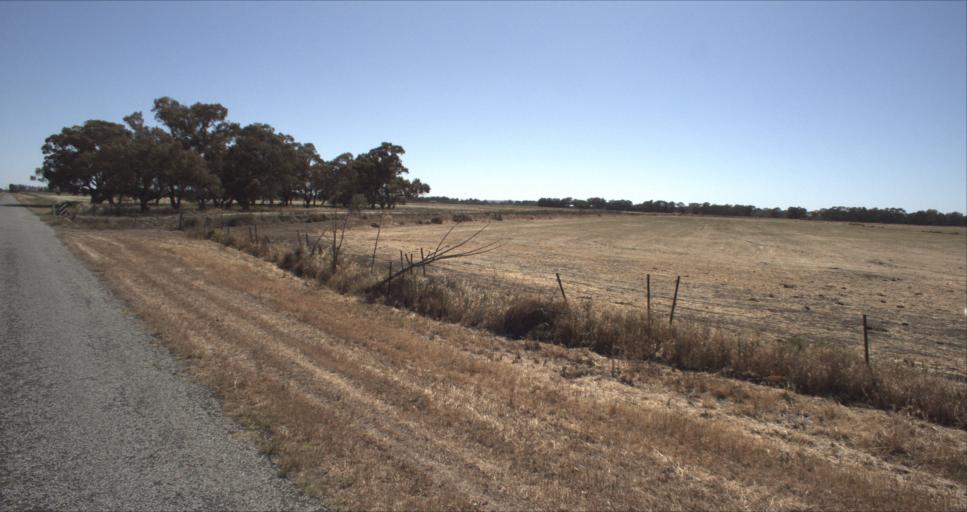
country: AU
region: New South Wales
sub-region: Leeton
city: Leeton
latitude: -34.5401
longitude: 146.3166
